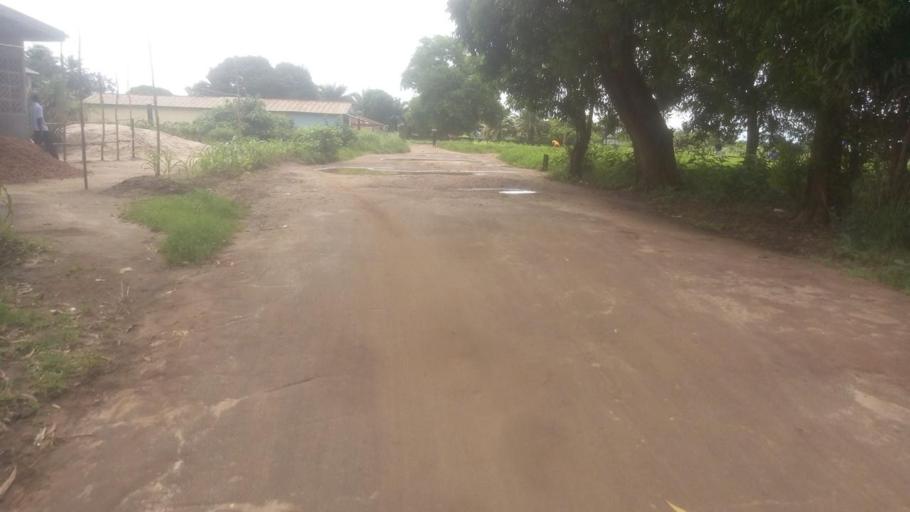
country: SL
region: Northern Province
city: Masoyila
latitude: 8.5985
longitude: -13.1863
